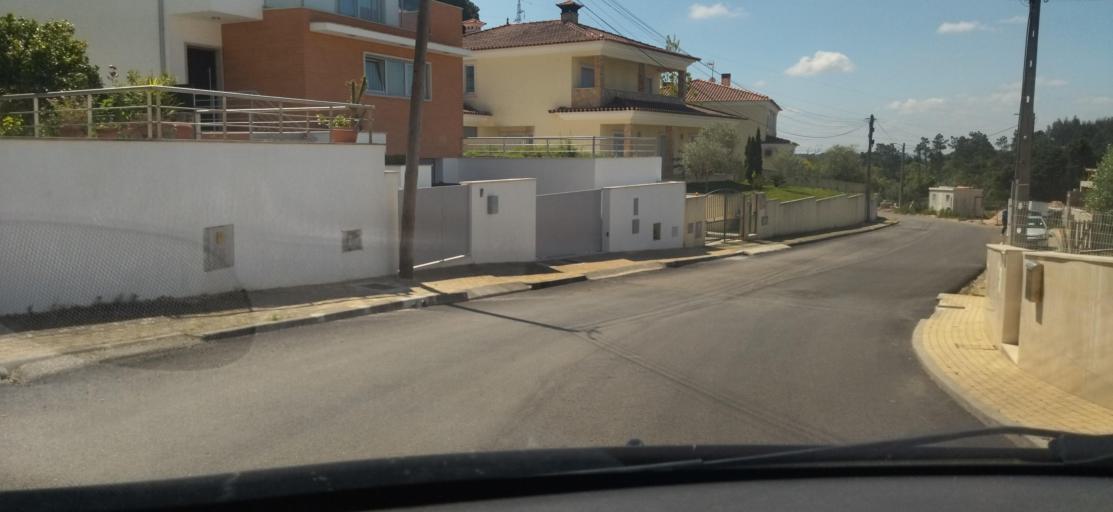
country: PT
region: Coimbra
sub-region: Coimbra
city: Coimbra
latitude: 40.1691
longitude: -8.4420
